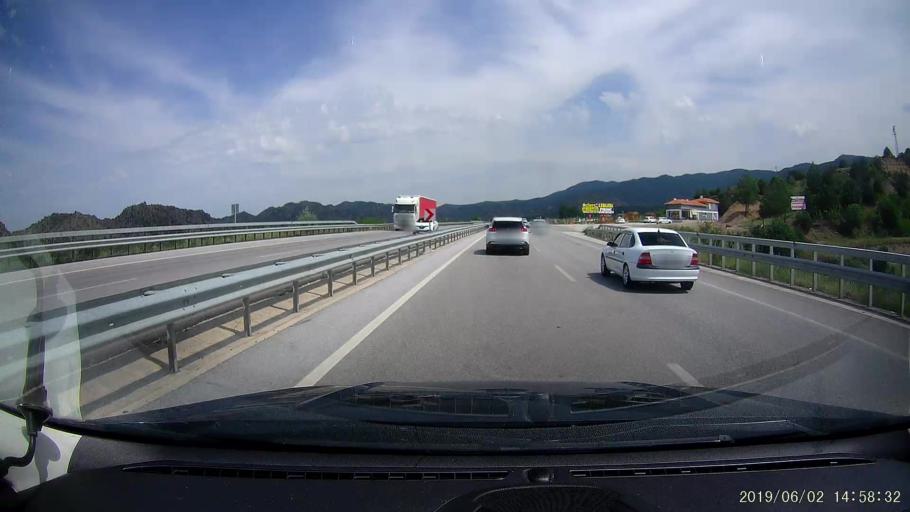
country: TR
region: Corum
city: Osmancik
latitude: 40.9807
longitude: 34.6783
